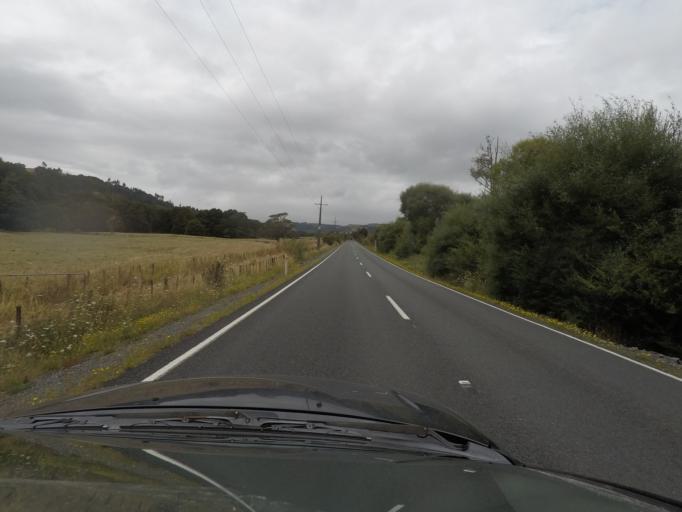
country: NZ
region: Auckland
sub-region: Auckland
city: Wellsford
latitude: -36.2927
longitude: 174.6229
